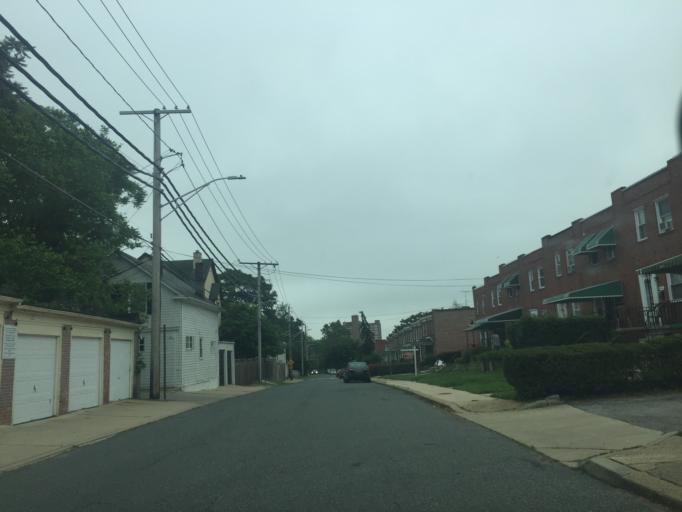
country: US
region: Maryland
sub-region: City of Baltimore
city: Baltimore
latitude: 39.3409
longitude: -76.6353
